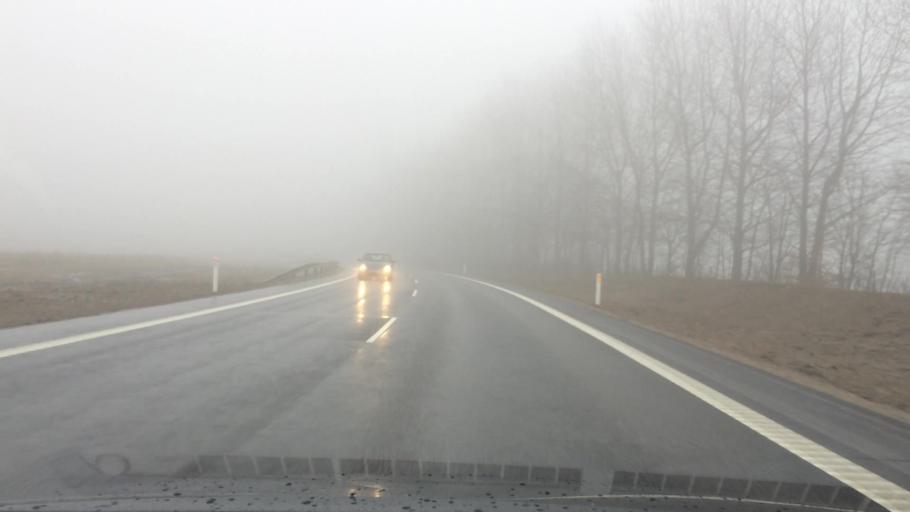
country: DK
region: Central Jutland
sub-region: Horsens Kommune
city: Horsens
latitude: 55.8619
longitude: 9.7962
